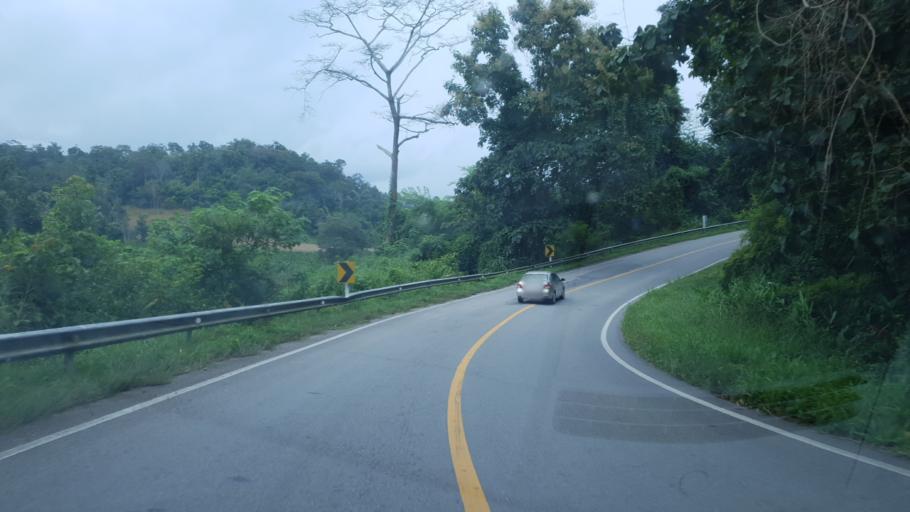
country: TH
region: Mae Hong Son
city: Khun Yuam
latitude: 18.7121
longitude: 97.9115
